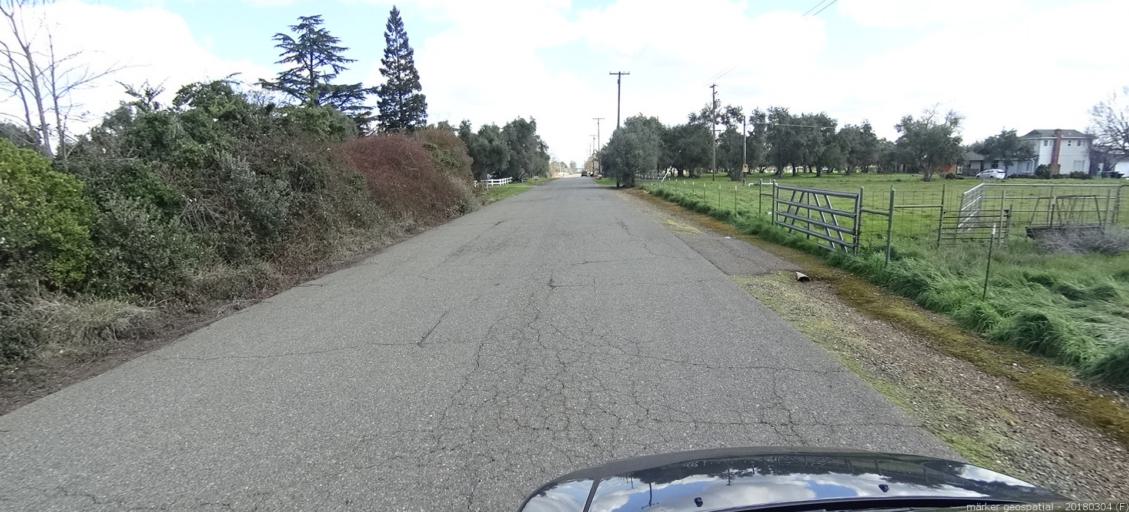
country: US
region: California
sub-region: Sacramento County
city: Vineyard
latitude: 38.4708
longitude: -121.3063
